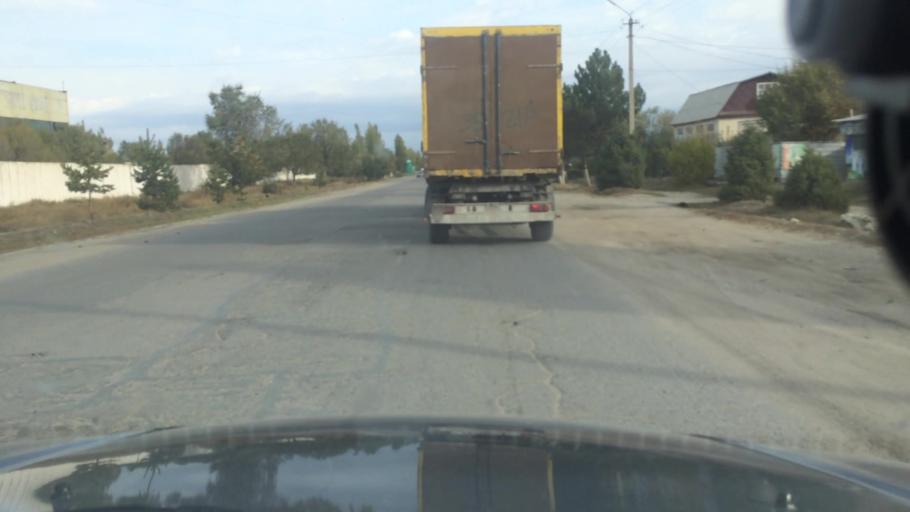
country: KG
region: Ysyk-Koel
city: Karakol
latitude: 42.5151
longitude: 78.3858
